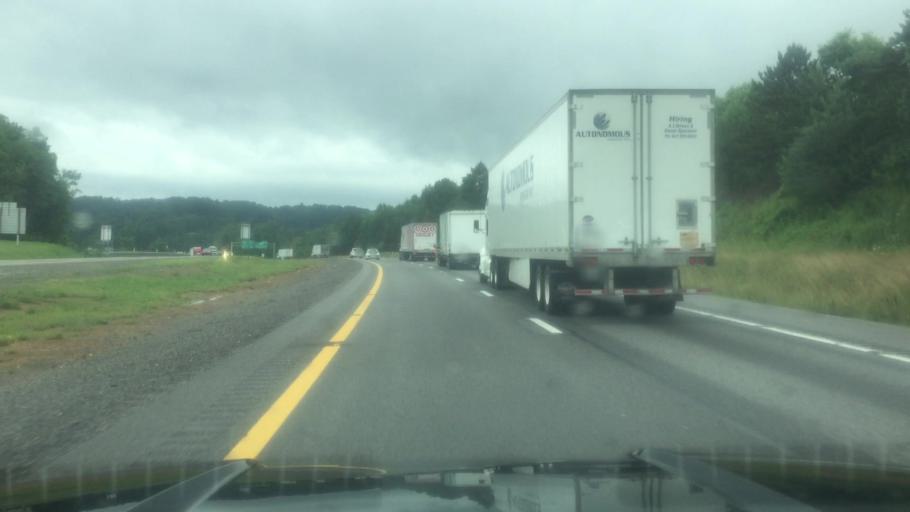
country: US
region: West Virginia
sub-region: Raleigh County
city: Prosperity
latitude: 37.8289
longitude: -81.2131
